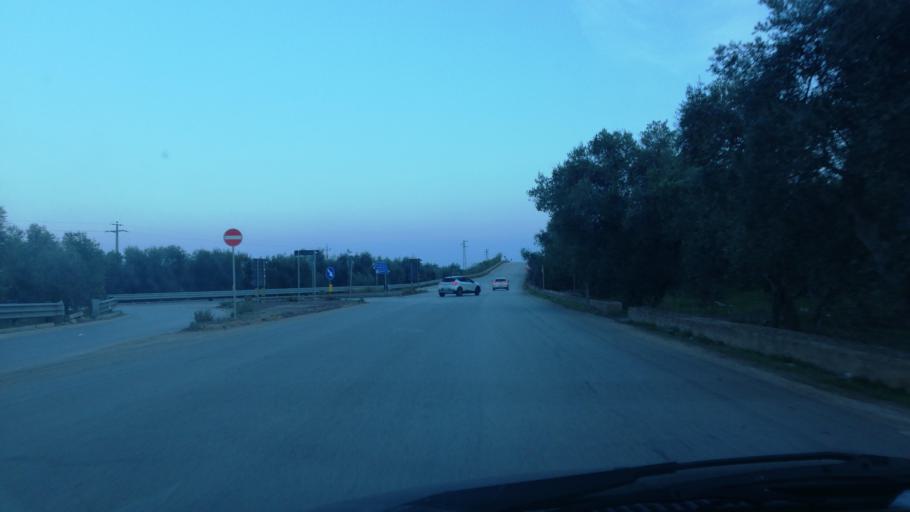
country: IT
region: Apulia
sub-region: Provincia di Bari
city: Bitonto
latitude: 41.1285
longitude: 16.7121
